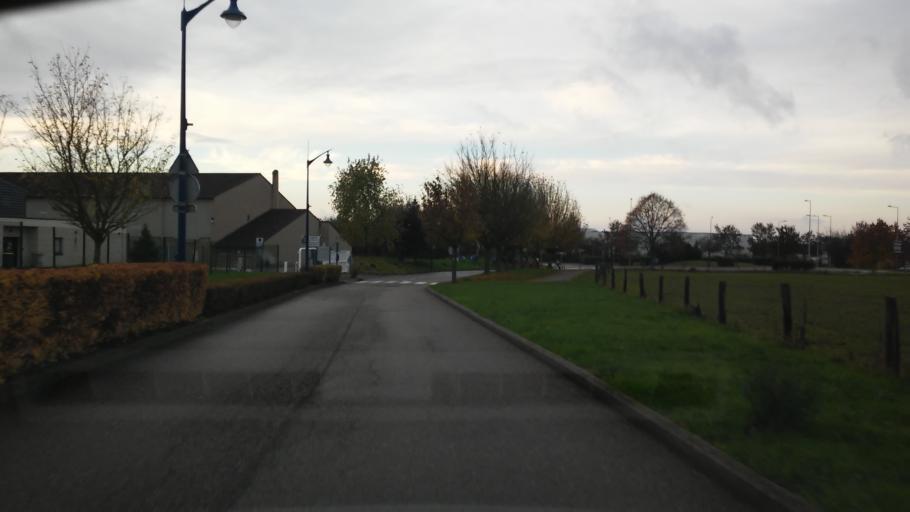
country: FR
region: Lorraine
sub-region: Departement de la Moselle
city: Ennery
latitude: 49.2284
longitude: 6.2175
